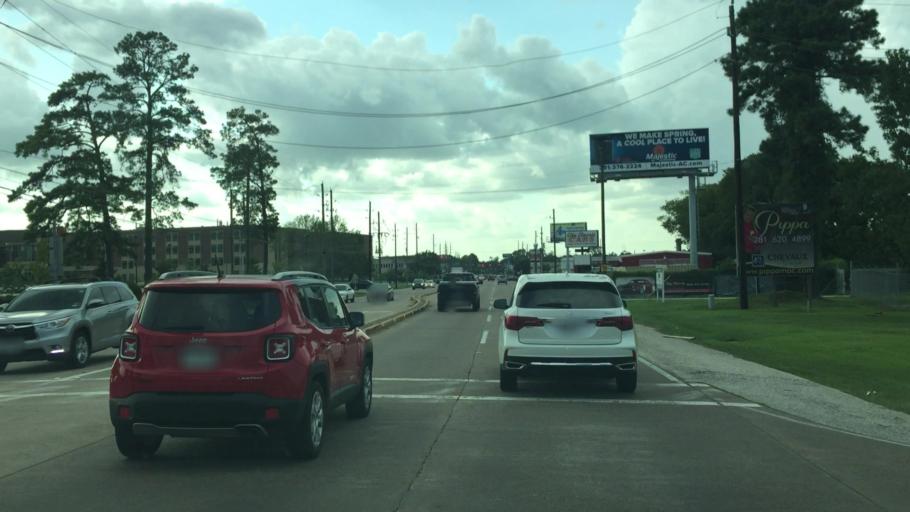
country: US
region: Texas
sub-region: Harris County
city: Hudson
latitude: 30.0185
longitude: -95.5206
